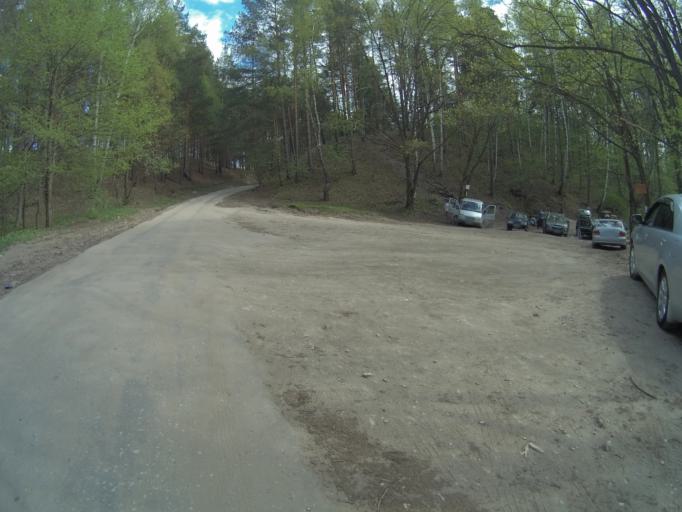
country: RU
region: Vladimir
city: Kommunar
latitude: 56.0649
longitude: 40.4295
